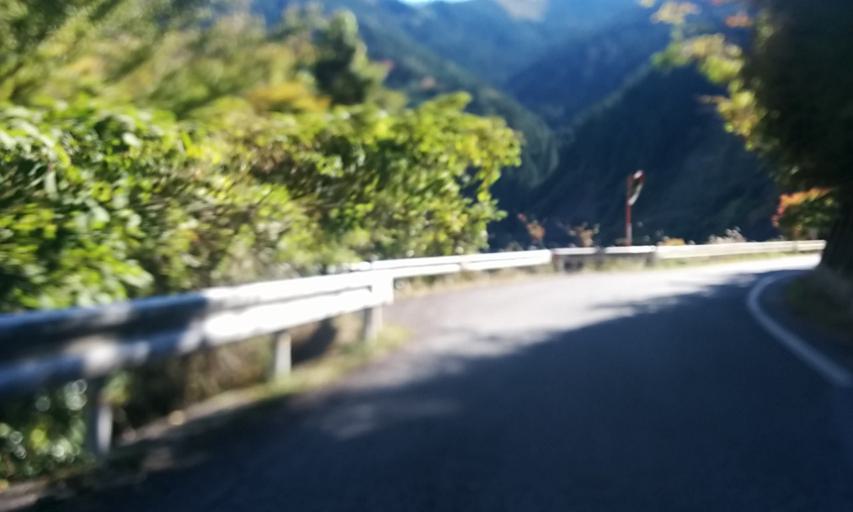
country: JP
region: Kyoto
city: Kameoka
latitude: 35.1296
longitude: 135.5648
